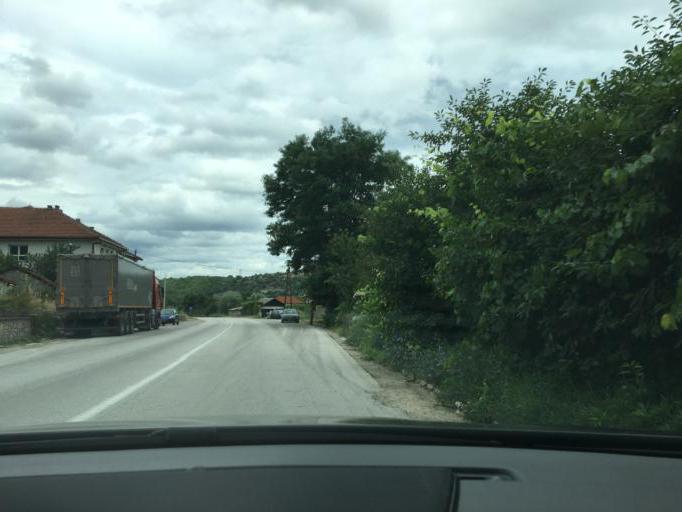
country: MK
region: Kriva Palanka
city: Kriva Palanka
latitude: 42.1765
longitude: 22.2506
